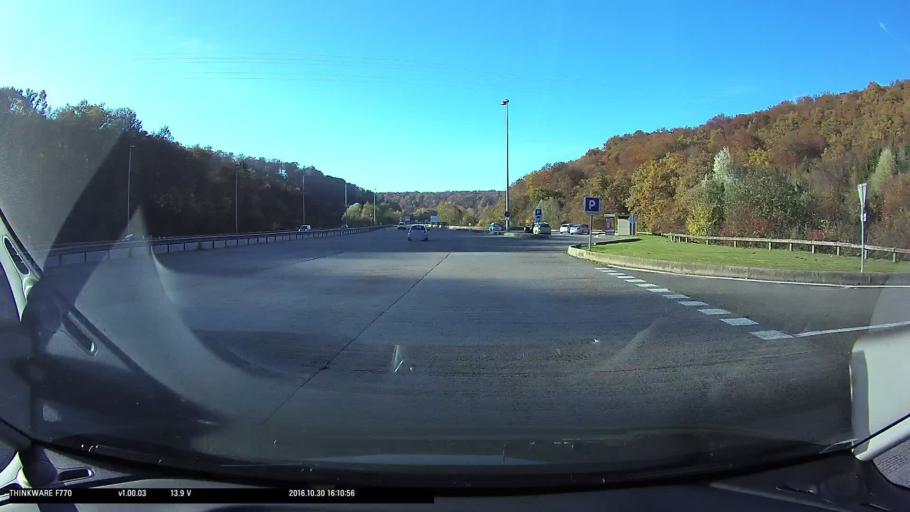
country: FR
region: Franche-Comte
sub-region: Departement du Doubs
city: Colombier-Fontaine
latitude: 47.4257
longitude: 6.6710
